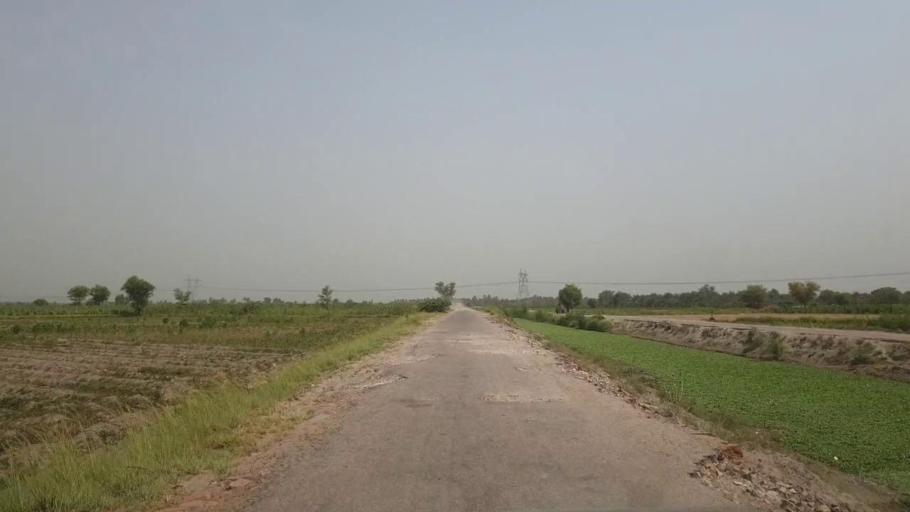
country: PK
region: Sindh
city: Gambat
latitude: 27.4086
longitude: 68.5503
